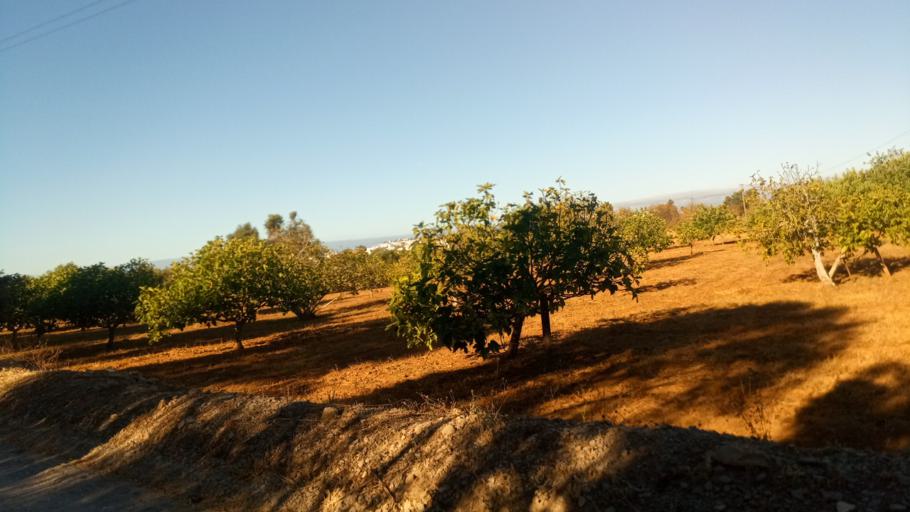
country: PT
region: Faro
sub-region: Tavira
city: Tavira
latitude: 37.1439
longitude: -7.5940
